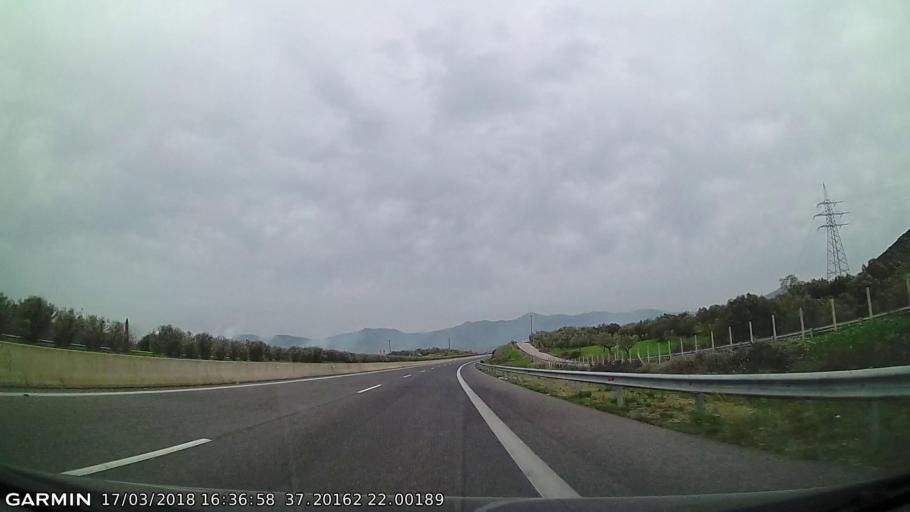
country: GR
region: Peloponnese
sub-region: Nomos Messinias
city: Meligalas
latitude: 37.2026
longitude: 22.0014
